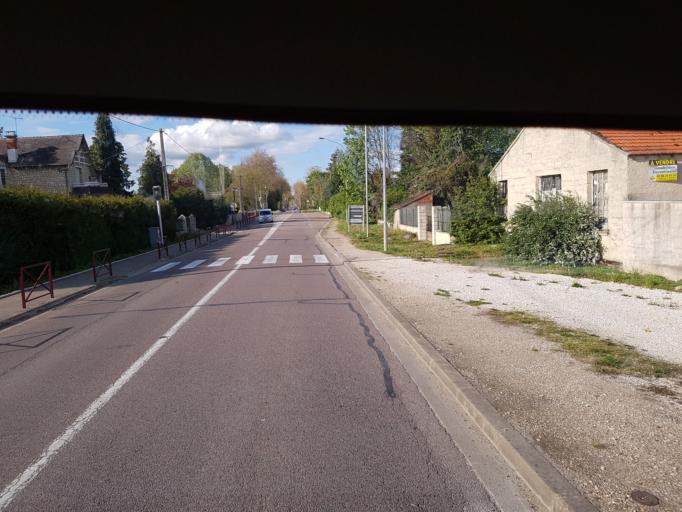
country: FR
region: Bourgogne
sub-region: Departement de l'Yonne
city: Saint-Florentin
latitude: 47.9841
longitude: 3.7327
